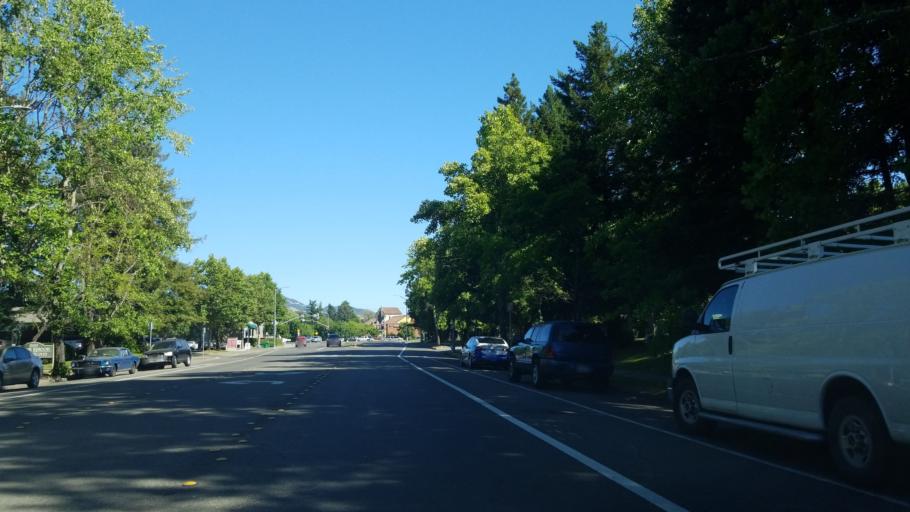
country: US
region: California
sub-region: Sonoma County
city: Santa Rosa
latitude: 38.4603
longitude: -122.6760
